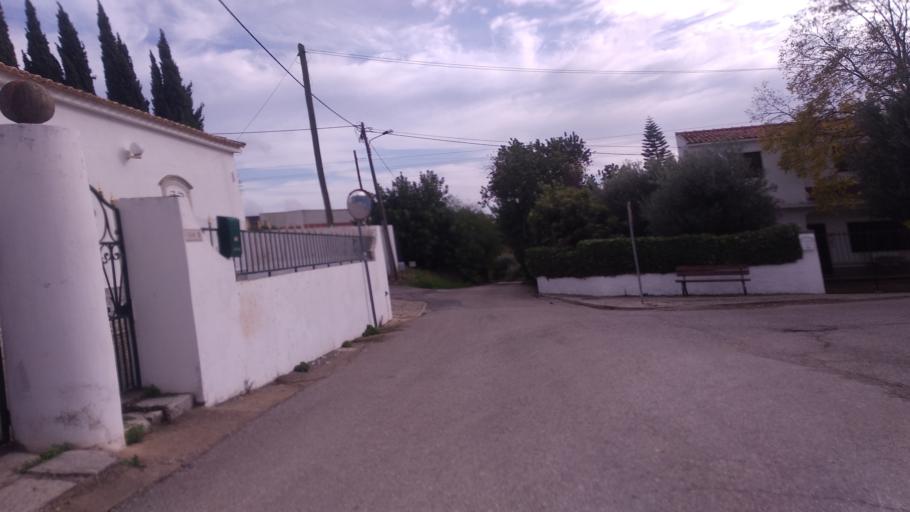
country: PT
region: Faro
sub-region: Sao Bras de Alportel
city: Sao Bras de Alportel
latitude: 37.1583
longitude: -7.8990
